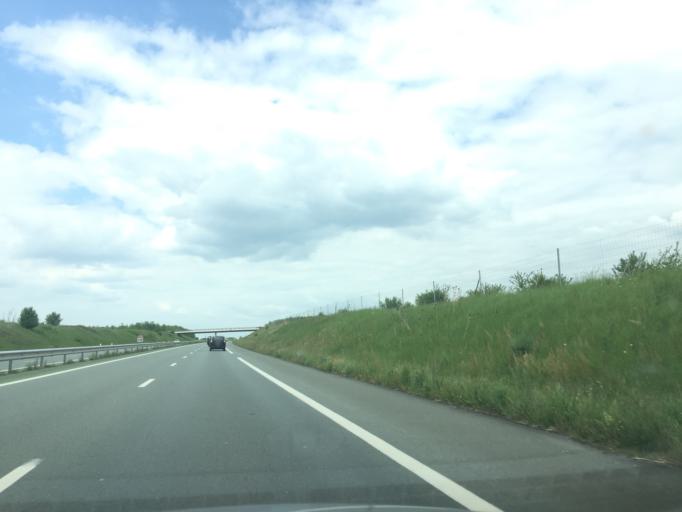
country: FR
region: Poitou-Charentes
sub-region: Departement des Deux-Sevres
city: Saint-Gelais
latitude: 46.3908
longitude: -0.3739
